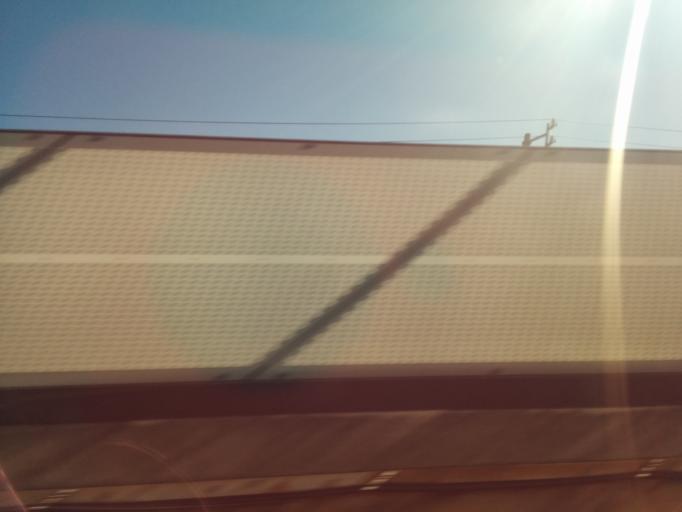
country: JP
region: Aichi
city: Chiryu
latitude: 34.9770
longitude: 137.0531
